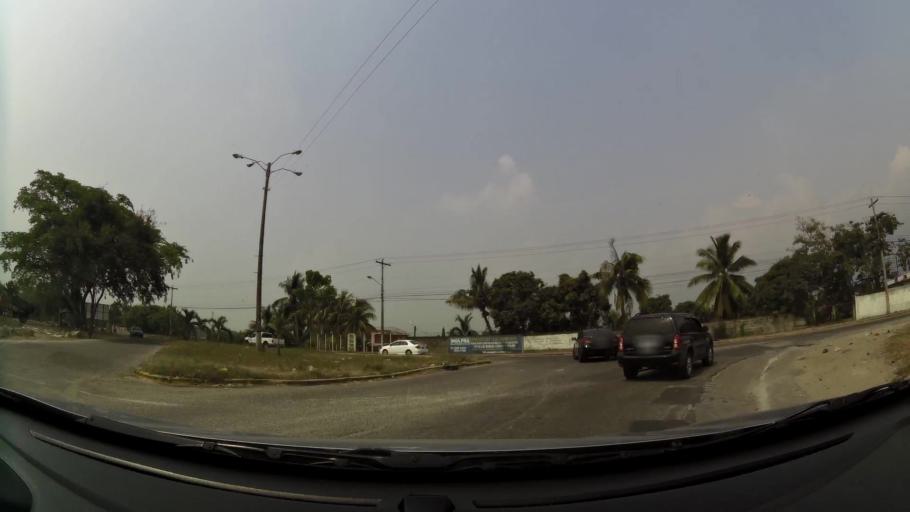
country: HN
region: Cortes
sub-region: San Pedro Sula
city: Pena Blanca
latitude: 15.5467
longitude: -88.0090
